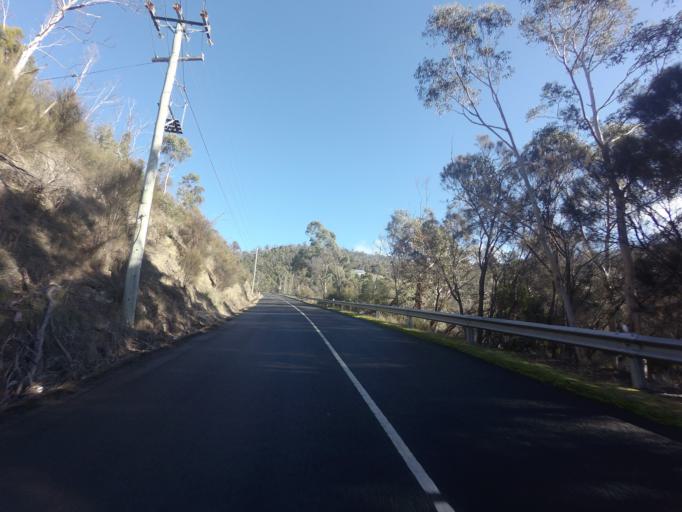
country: AU
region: Tasmania
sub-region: Glenorchy
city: Berriedale
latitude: -42.8205
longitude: 147.2137
